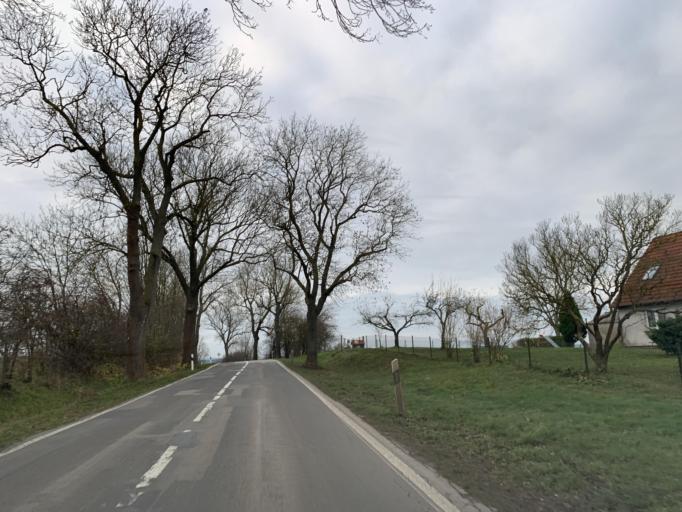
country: DE
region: Mecklenburg-Vorpommern
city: Blankensee
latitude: 53.3913
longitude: 13.3070
